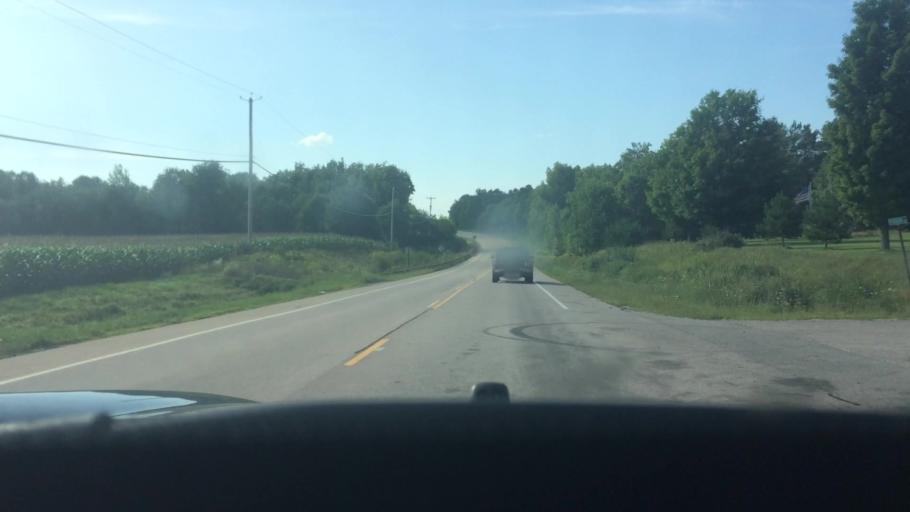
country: US
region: New York
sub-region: Franklin County
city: Malone
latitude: 44.8485
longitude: -74.1983
